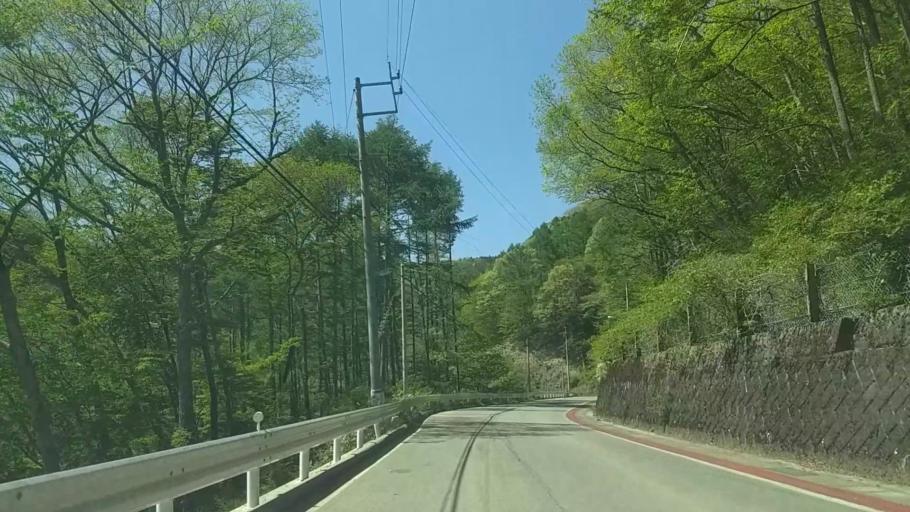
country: JP
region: Yamanashi
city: Nirasaki
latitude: 35.9191
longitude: 138.4462
